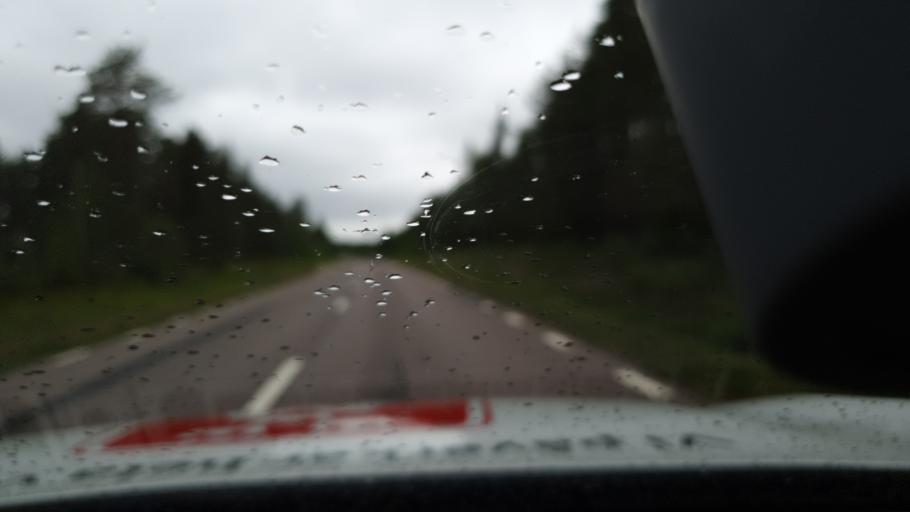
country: FI
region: Lapland
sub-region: Torniolaakso
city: Pello
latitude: 66.9920
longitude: 23.7764
